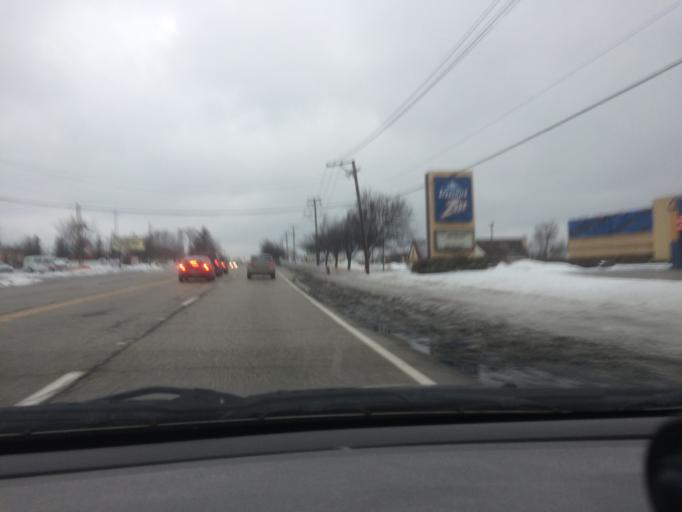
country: US
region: Illinois
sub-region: DuPage County
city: Bloomingdale
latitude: 41.9675
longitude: -88.1096
